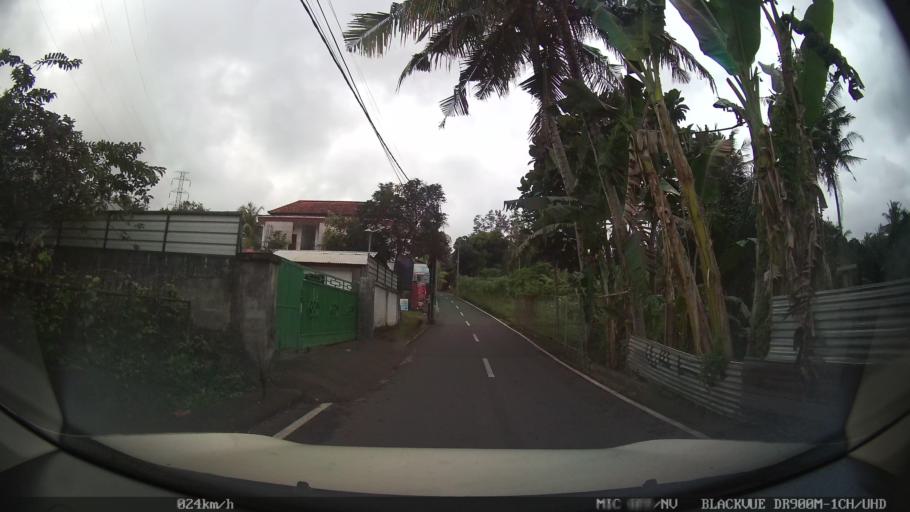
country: ID
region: Bali
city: Banjar Mambalkajanan
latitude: -8.5608
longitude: 115.2141
